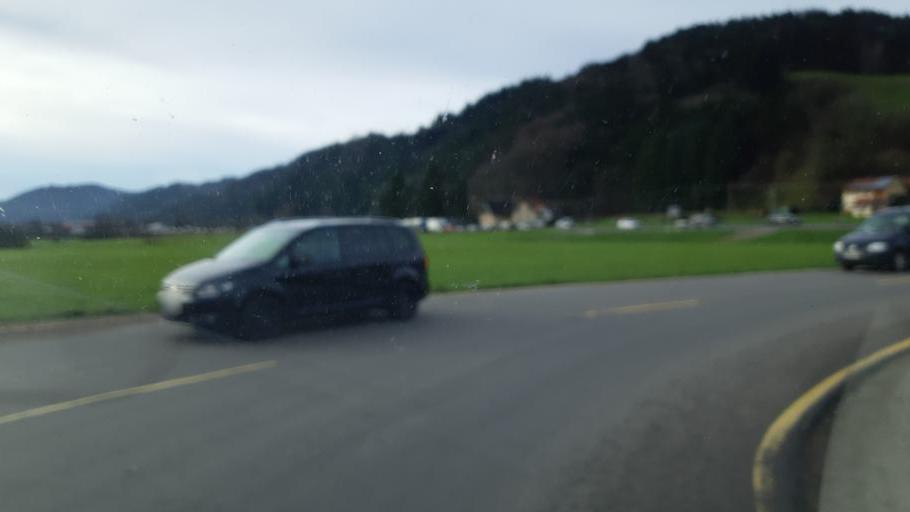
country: DE
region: Baden-Wuerttemberg
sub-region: Freiburg Region
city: Elzach
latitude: 48.1507
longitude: 8.0365
